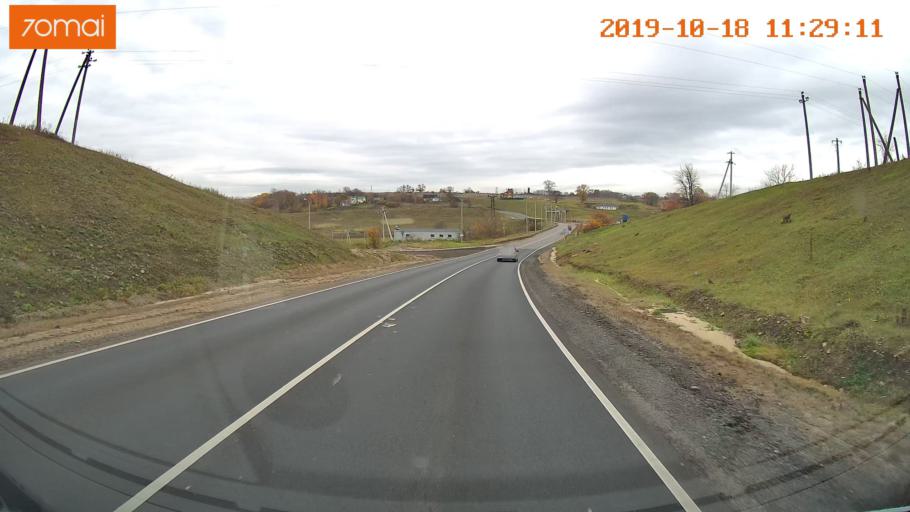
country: RU
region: Rjazan
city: Oktyabr'skiy
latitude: 54.1574
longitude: 38.6736
